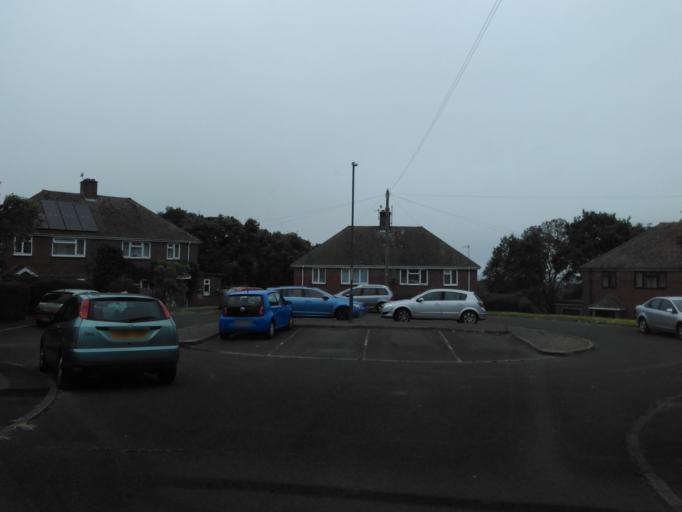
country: GB
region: England
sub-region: Kent
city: Chartham
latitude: 51.2515
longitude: 1.0125
